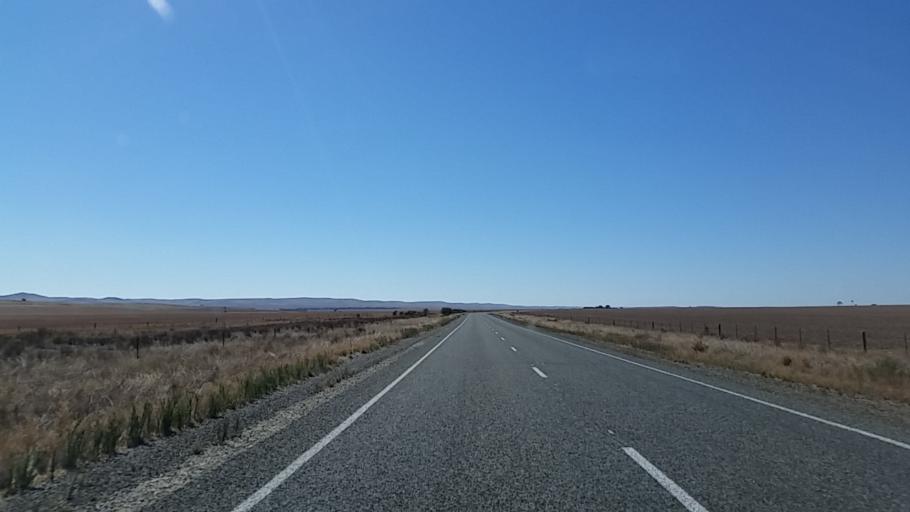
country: AU
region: South Australia
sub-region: Northern Areas
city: Jamestown
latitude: -33.2739
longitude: 138.8684
